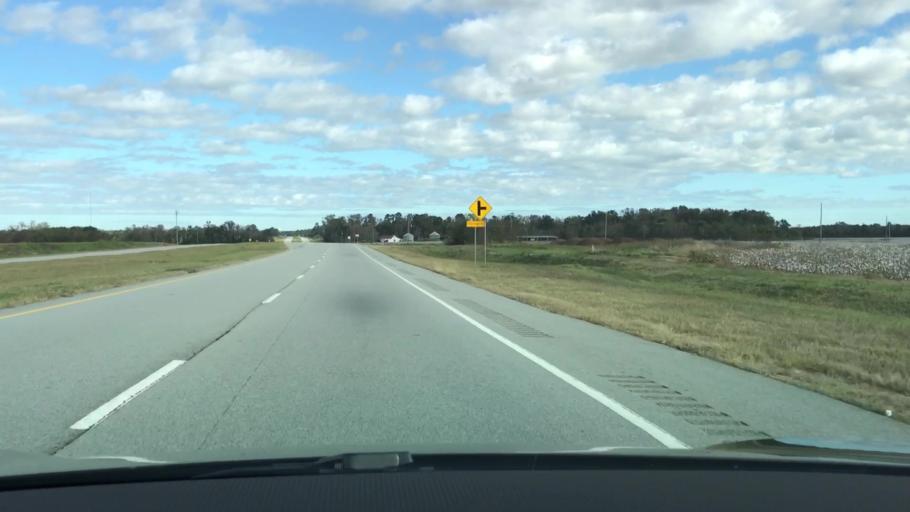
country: US
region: Georgia
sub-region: Jefferson County
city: Wadley
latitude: 32.8277
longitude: -82.4025
